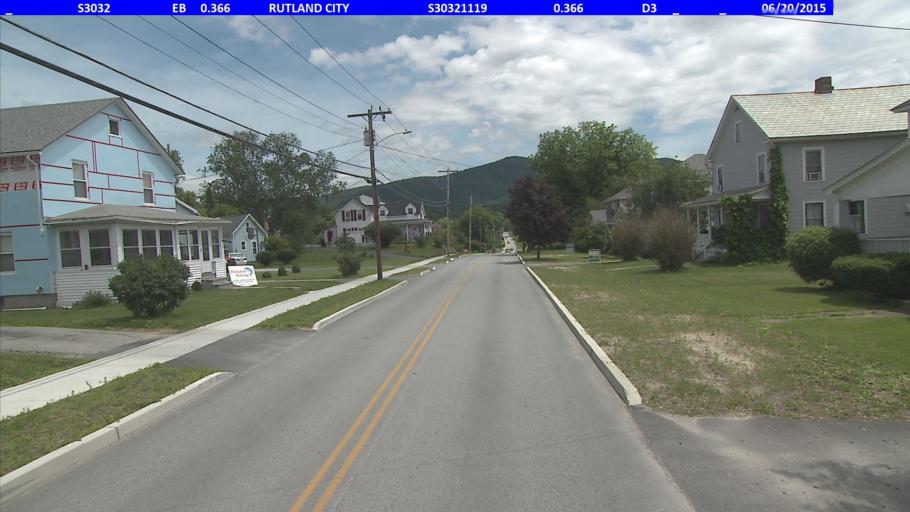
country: US
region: Vermont
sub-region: Rutland County
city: Rutland
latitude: 43.6057
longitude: -72.9646
